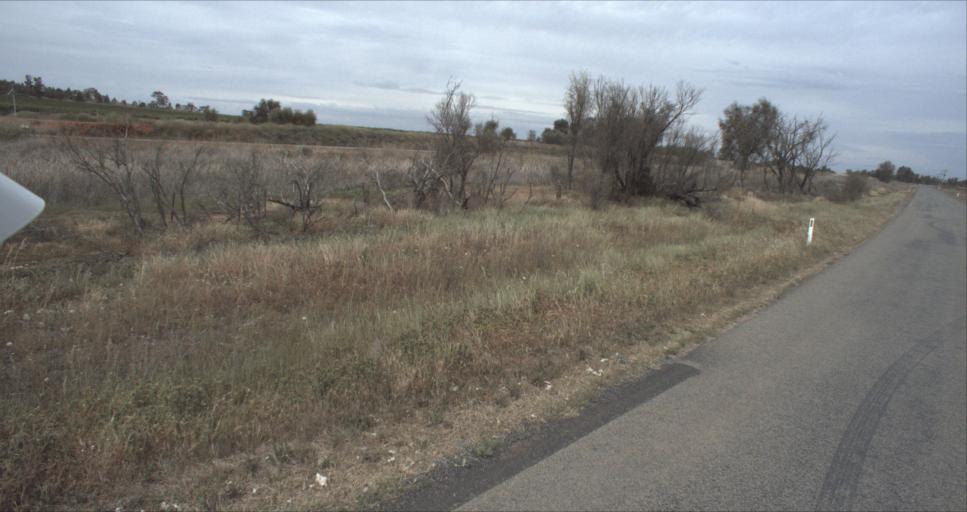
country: AU
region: New South Wales
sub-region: Leeton
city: Leeton
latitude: -34.4346
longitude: 146.3764
